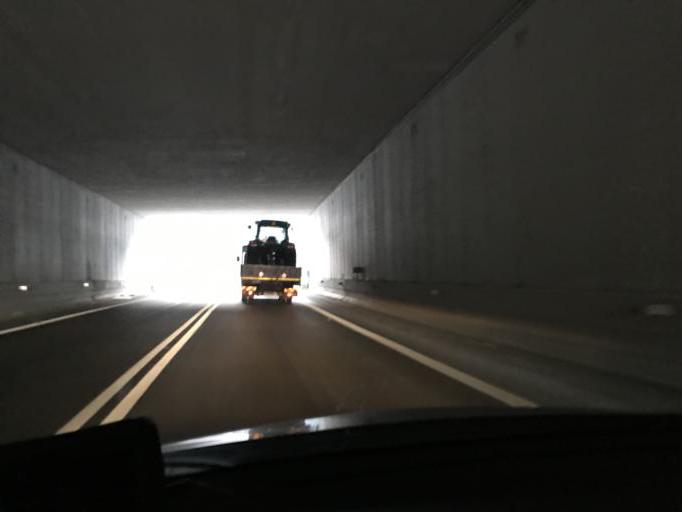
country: IT
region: Umbria
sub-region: Provincia di Terni
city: Terni
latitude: 42.5548
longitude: 12.6979
